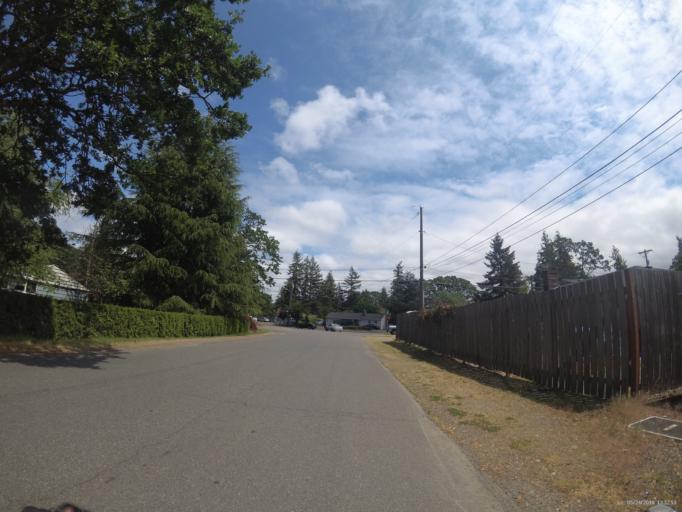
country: US
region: Washington
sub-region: Pierce County
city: Lakewood
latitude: 47.1795
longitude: -122.5280
